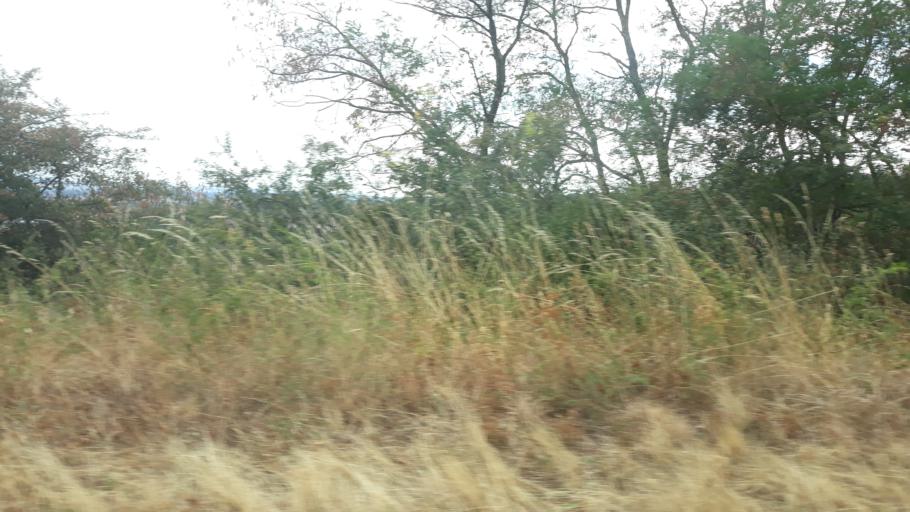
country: FR
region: Bourgogne
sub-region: Departement de Saone-et-Loire
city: Le Creusot
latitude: 46.8141
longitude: 4.4248
